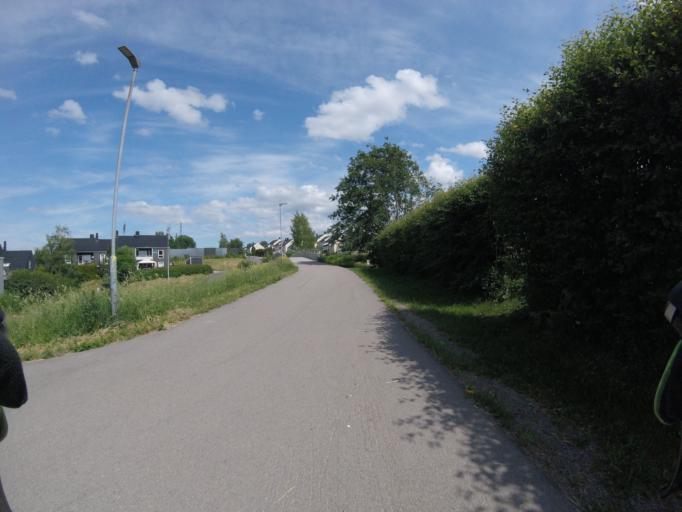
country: NO
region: Akershus
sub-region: Skedsmo
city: Lillestrom
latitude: 59.9872
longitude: 11.0365
